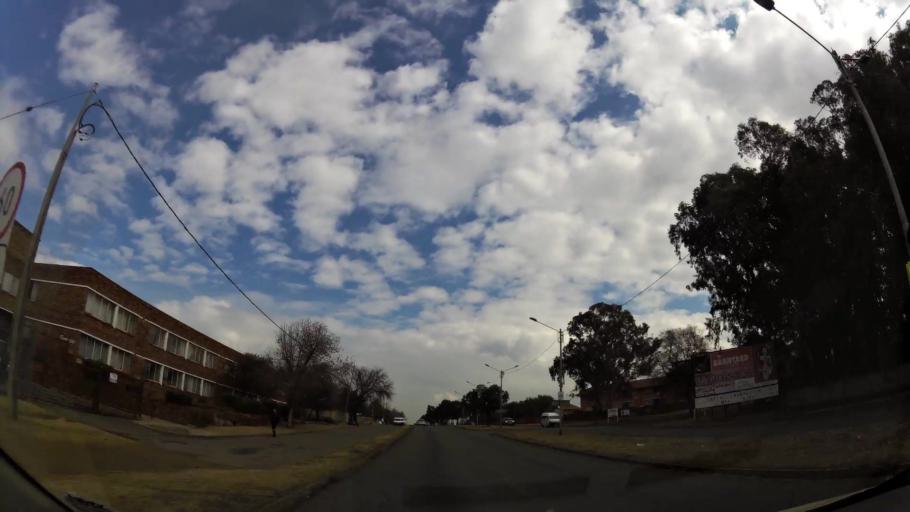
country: ZA
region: Gauteng
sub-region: Sedibeng District Municipality
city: Vereeniging
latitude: -26.6587
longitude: 27.9550
